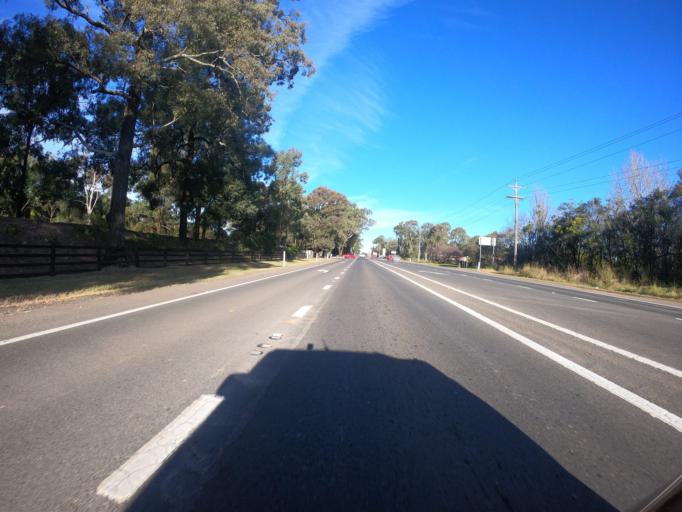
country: AU
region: New South Wales
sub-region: Hawkesbury
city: South Windsor
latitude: -33.6626
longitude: 150.7987
